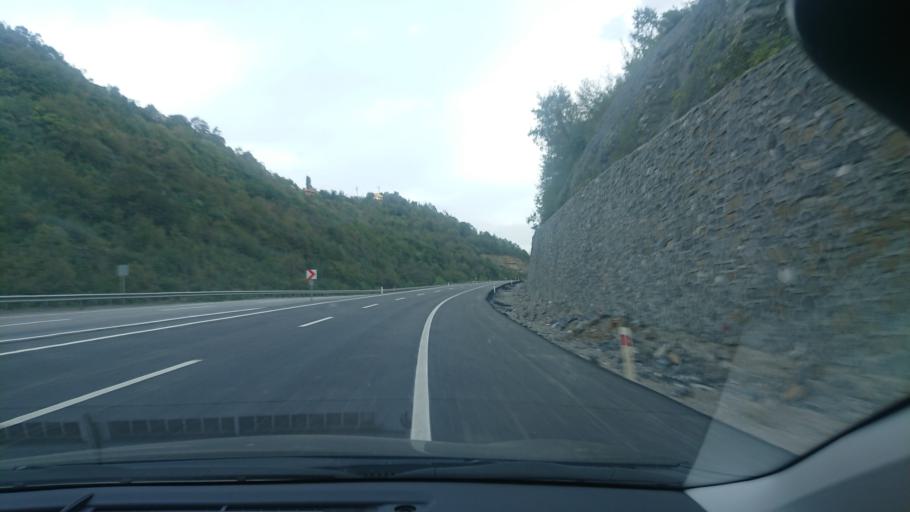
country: TR
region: Zonguldak
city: Beycuma
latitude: 41.3888
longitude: 31.9361
